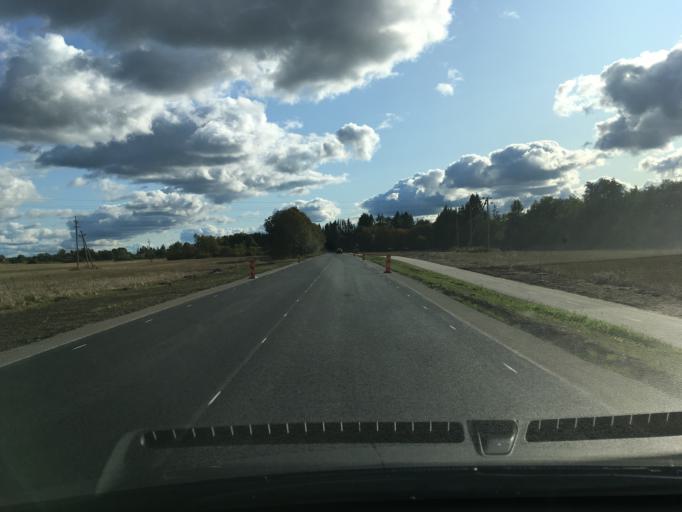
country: EE
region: Harju
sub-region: Joelaehtme vald
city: Loo
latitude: 59.4216
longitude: 24.9436
